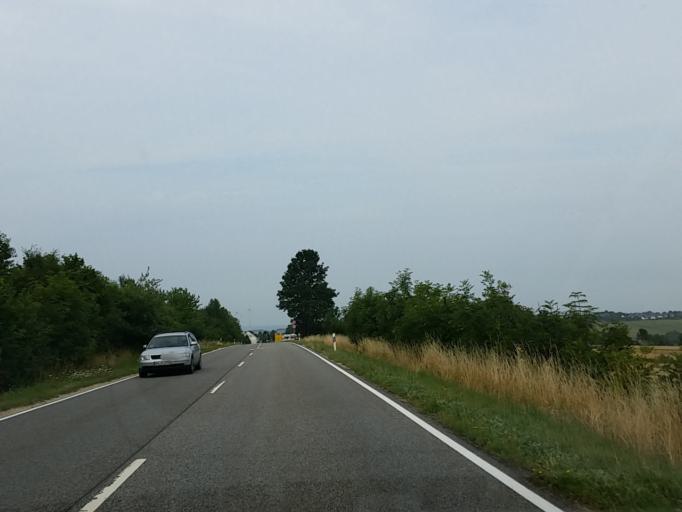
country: DE
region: Rheinland-Pfalz
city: Farschweiler
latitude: 49.7236
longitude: 6.8090
